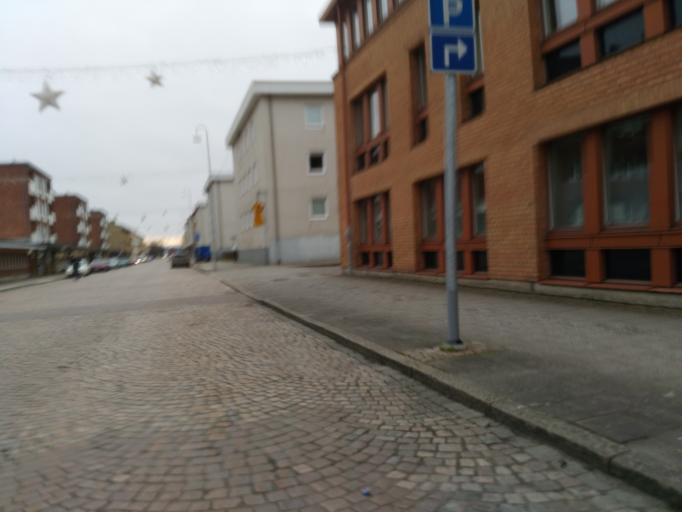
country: SE
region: Vaestra Goetaland
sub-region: Lidkopings Kommun
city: Lidkoping
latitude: 58.5021
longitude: 13.1638
